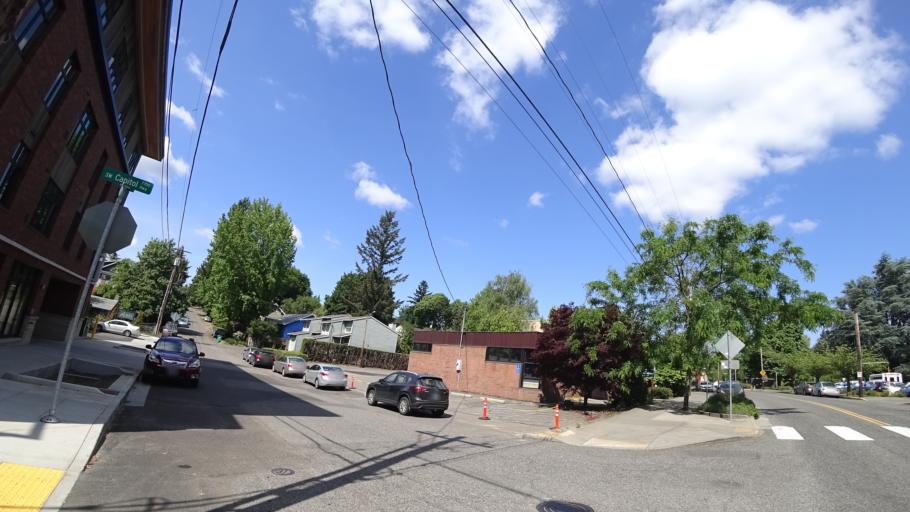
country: US
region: Oregon
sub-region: Washington County
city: Garden Home-Whitford
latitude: 45.4686
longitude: -122.7103
